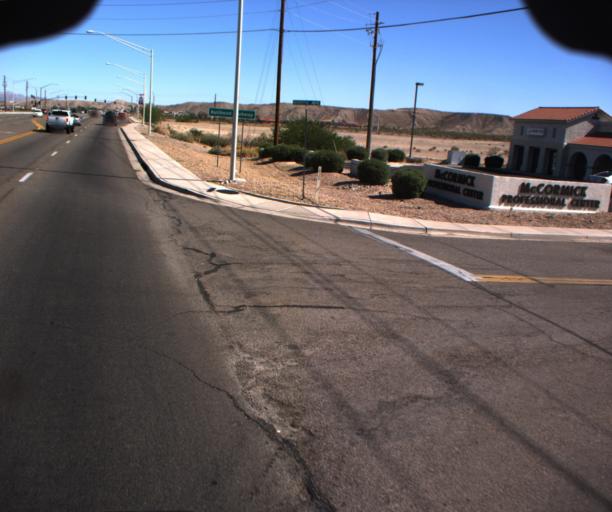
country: US
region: Arizona
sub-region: Mohave County
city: Bullhead City
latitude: 35.0538
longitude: -114.5890
